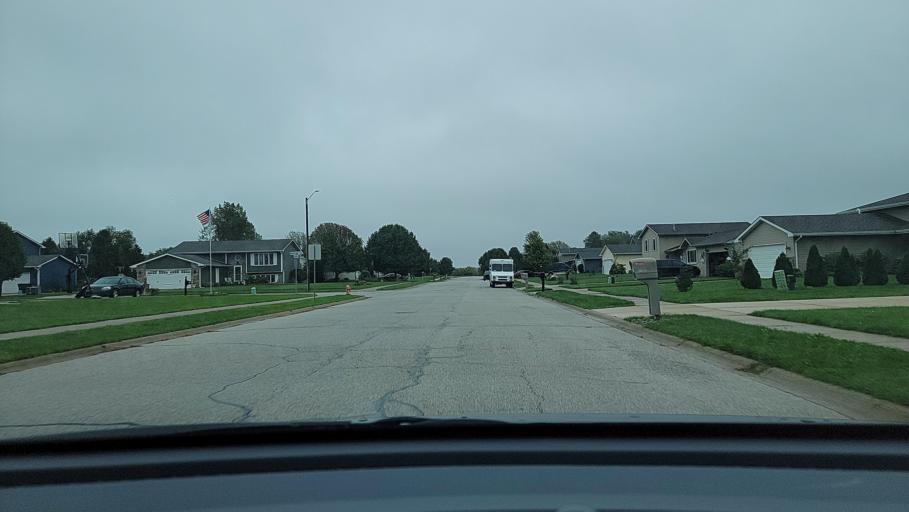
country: US
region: Indiana
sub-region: Porter County
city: Portage
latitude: 41.5437
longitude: -87.1902
